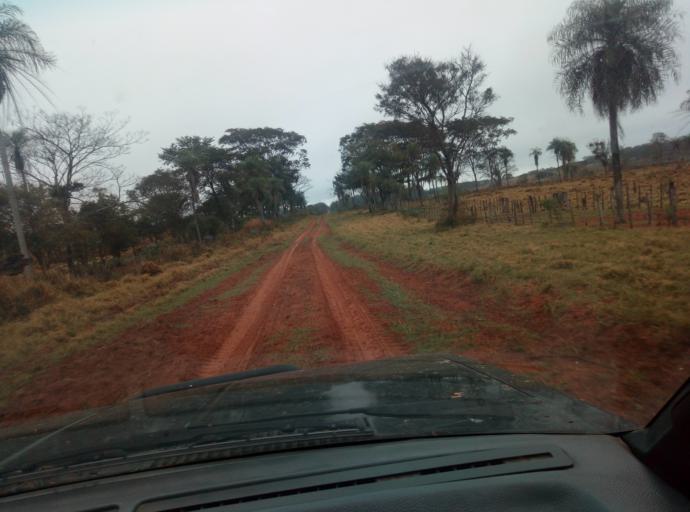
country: PY
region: Caaguazu
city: Carayao
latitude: -25.1935
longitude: -56.3293
